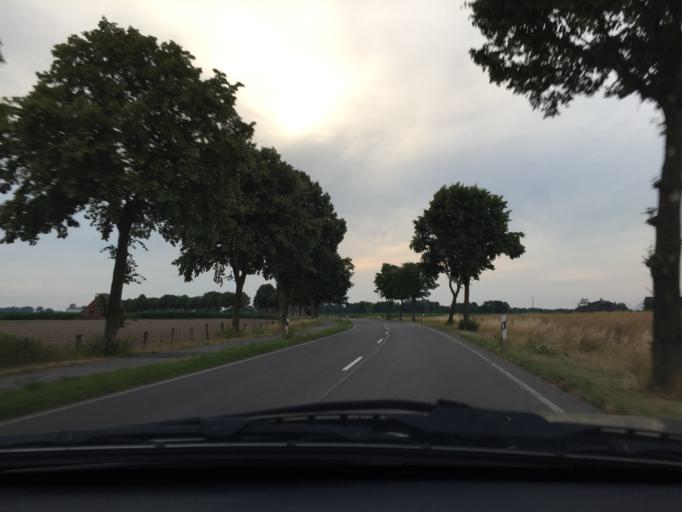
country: DE
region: North Rhine-Westphalia
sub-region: Regierungsbezirk Dusseldorf
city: Emmerich
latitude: 51.7769
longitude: 6.2404
